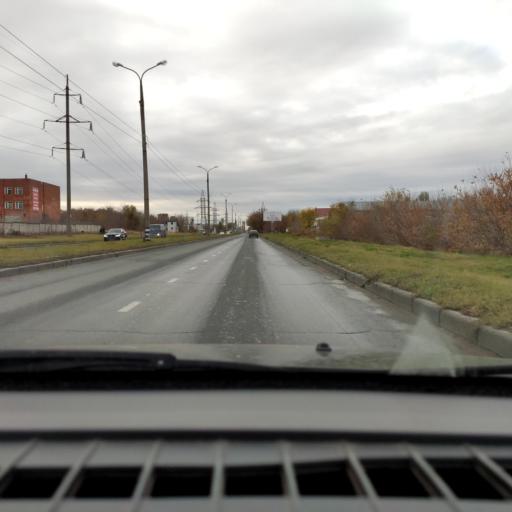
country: RU
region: Samara
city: Tol'yatti
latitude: 53.5570
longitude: 49.3193
